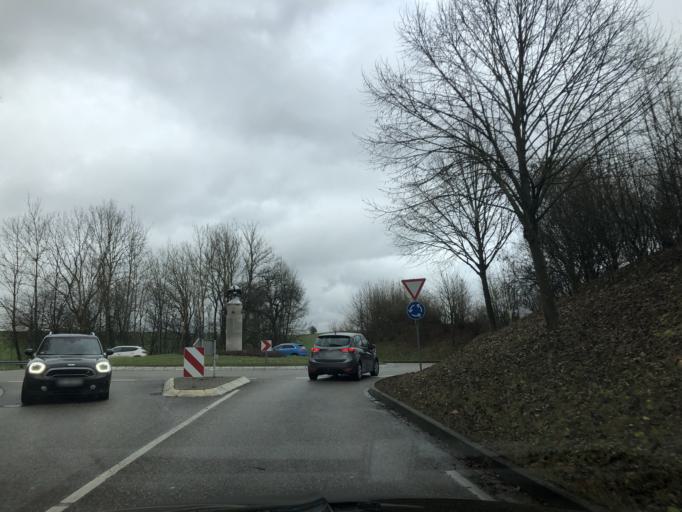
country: DE
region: Baden-Wuerttemberg
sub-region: Karlsruhe Region
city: Bammental
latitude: 49.3208
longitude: 8.7621
